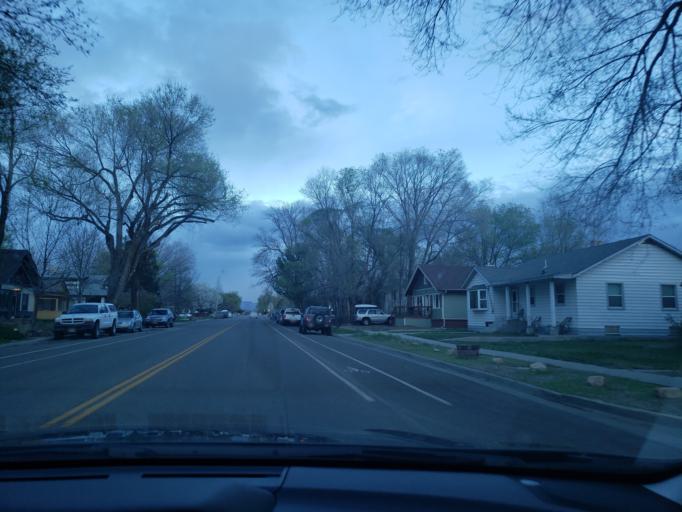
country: US
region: Colorado
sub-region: Mesa County
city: Fruita
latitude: 39.1589
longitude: -108.7266
